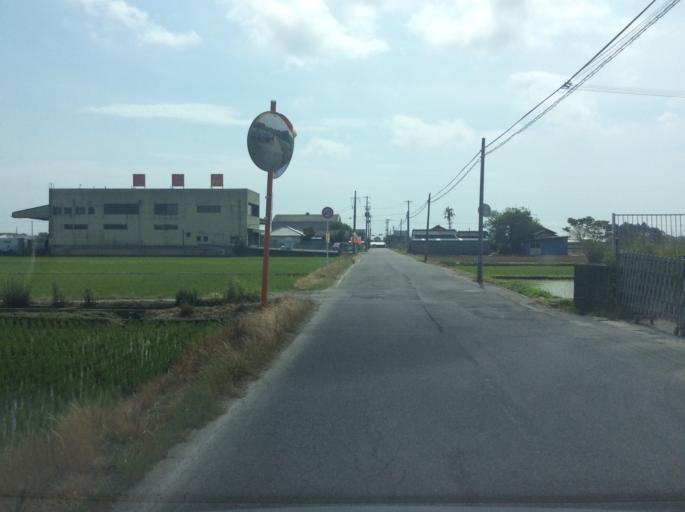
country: JP
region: Fukushima
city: Iwaki
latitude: 37.0638
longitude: 140.9466
